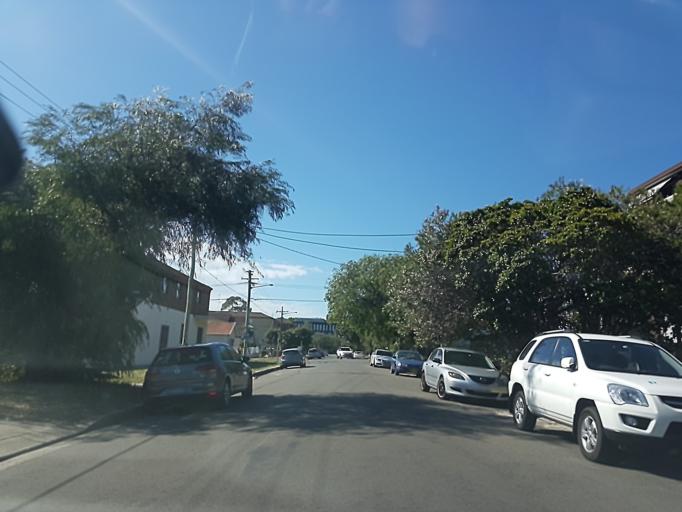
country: AU
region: New South Wales
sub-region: Randwick
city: Kingsford
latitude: -33.9218
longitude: 151.2300
